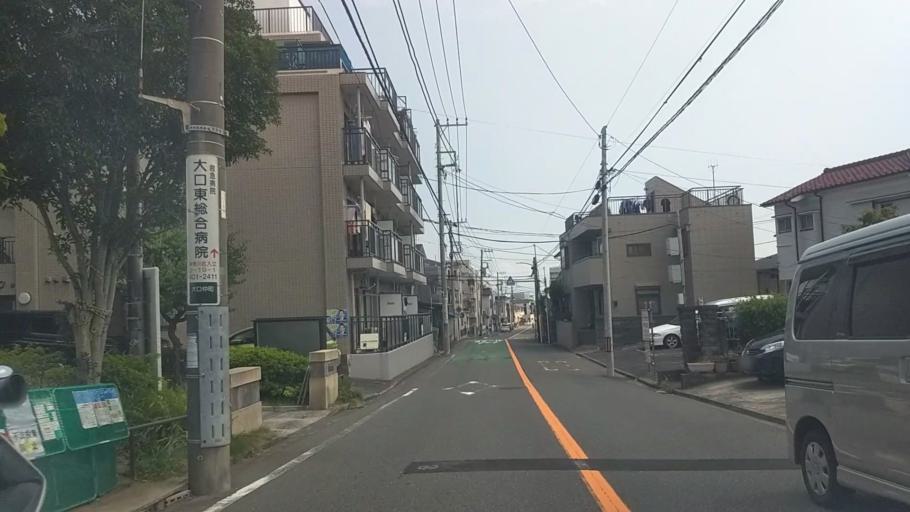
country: JP
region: Kanagawa
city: Yokohama
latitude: 35.4939
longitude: 139.6390
